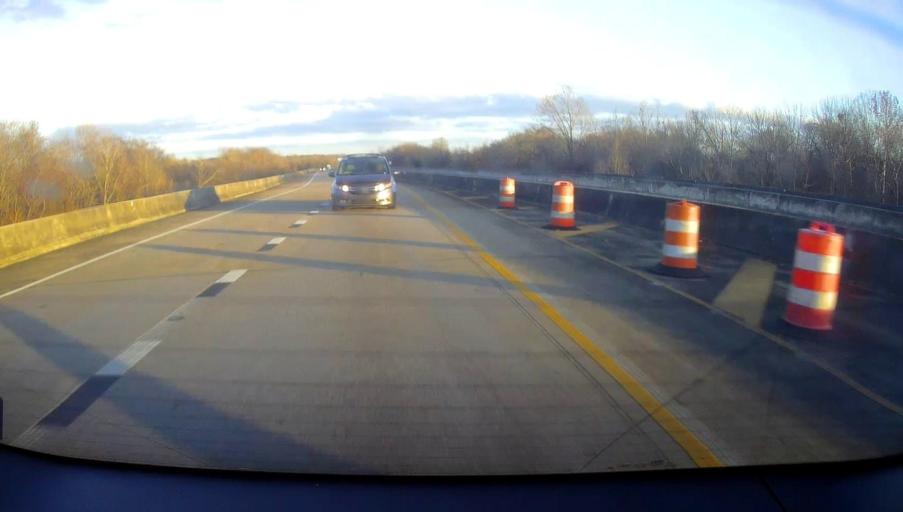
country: US
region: Alabama
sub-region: Etowah County
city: Attalla
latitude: 34.0048
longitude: -86.0711
